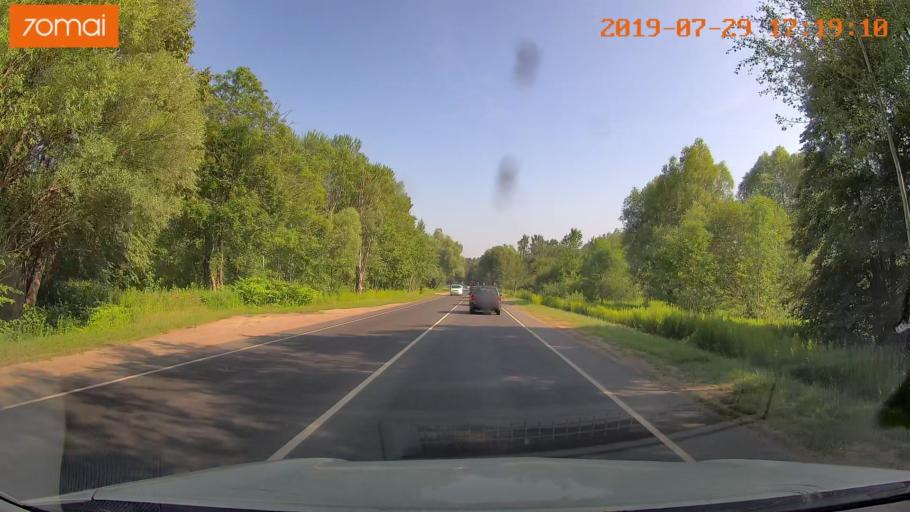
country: RU
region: Kaliningrad
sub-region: Gorod Kaliningrad
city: Kaliningrad
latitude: 54.7724
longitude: 20.4222
